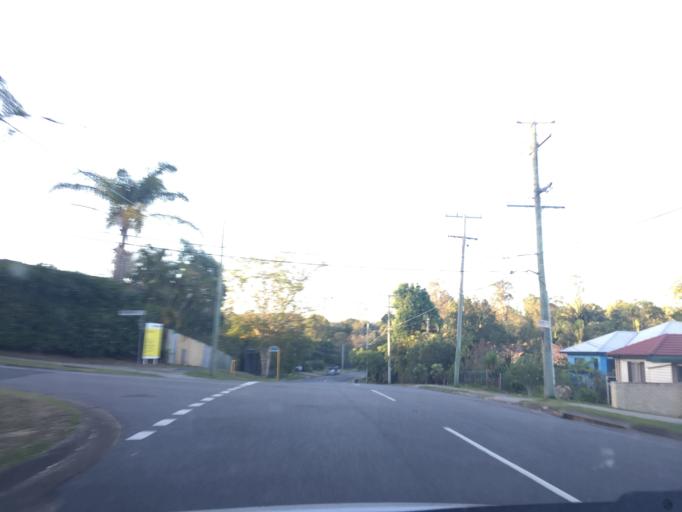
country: AU
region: Queensland
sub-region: Moreton Bay
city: Ferny Hills
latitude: -27.4461
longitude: 152.9406
